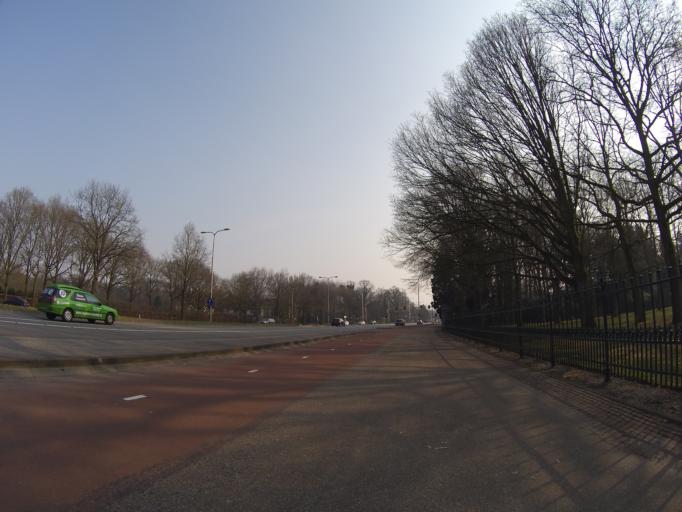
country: NL
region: Utrecht
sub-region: Gemeente Baarn
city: Baarn
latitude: 52.1937
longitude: 5.2812
